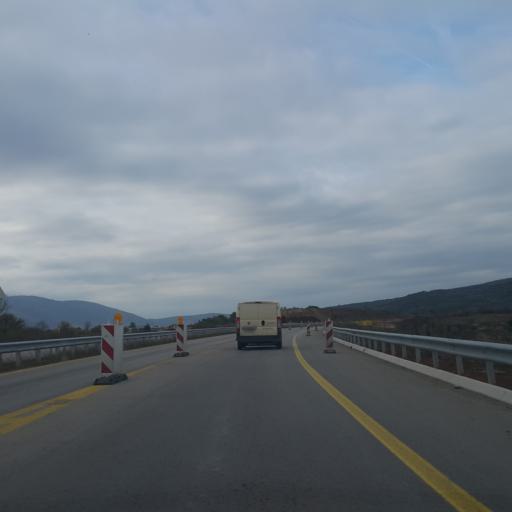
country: RS
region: Central Serbia
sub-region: Pirotski Okrug
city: Bela Palanka
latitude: 43.2250
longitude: 22.3894
